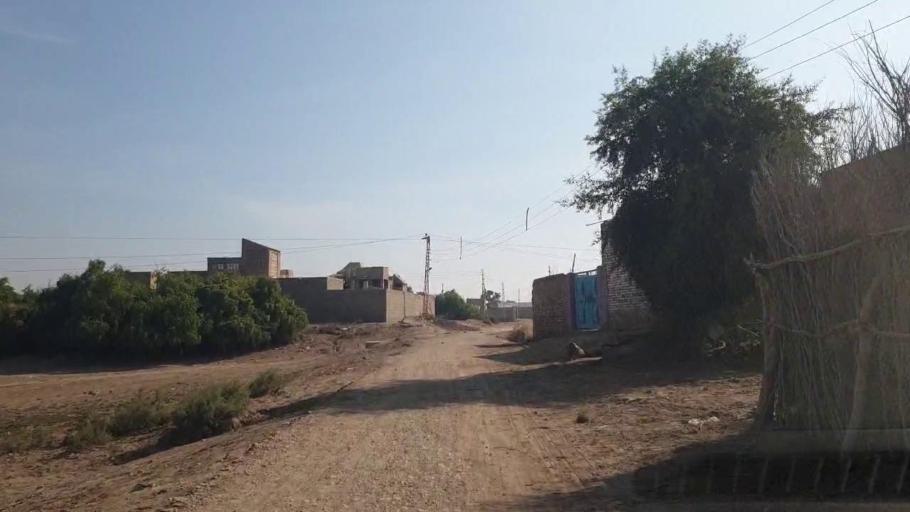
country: PK
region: Sindh
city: Matiari
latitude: 25.6445
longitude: 68.3528
